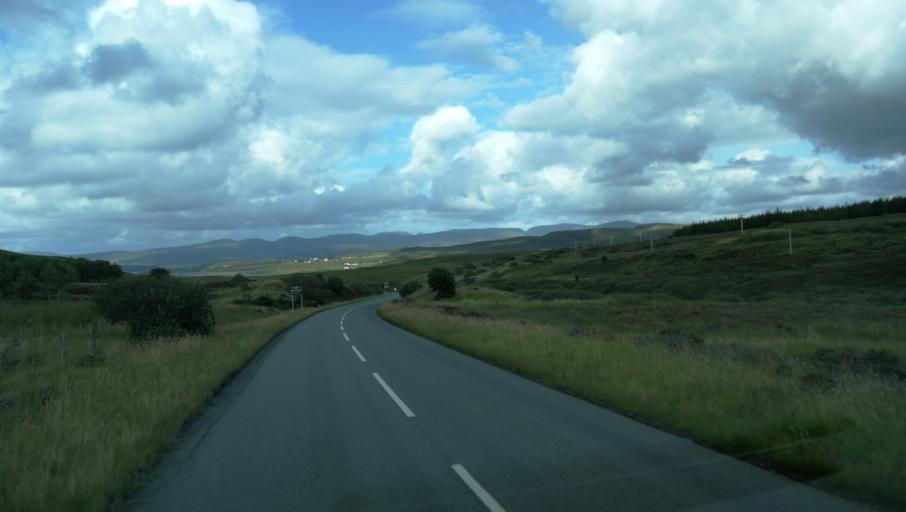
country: GB
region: Scotland
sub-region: Highland
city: Isle of Skye
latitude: 57.4696
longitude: -6.4754
